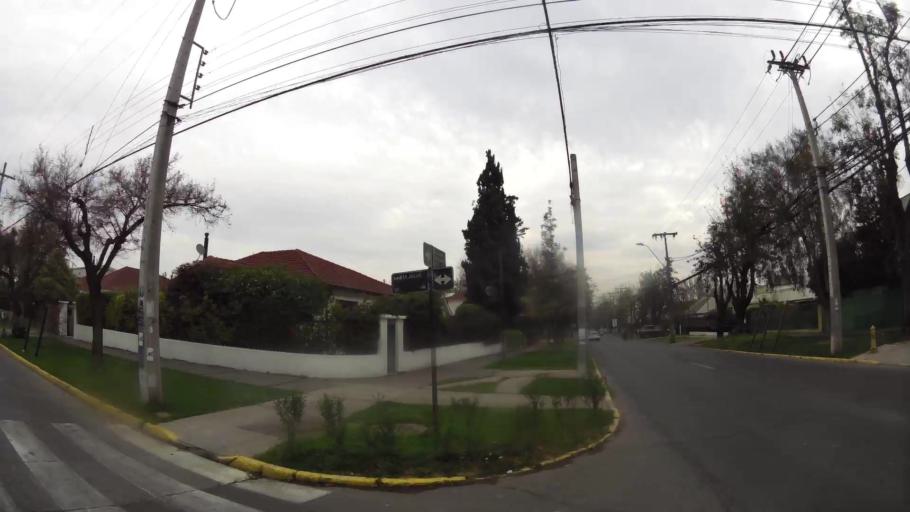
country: CL
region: Santiago Metropolitan
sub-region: Provincia de Santiago
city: Villa Presidente Frei, Nunoa, Santiago, Chile
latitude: -33.4595
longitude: -70.5903
